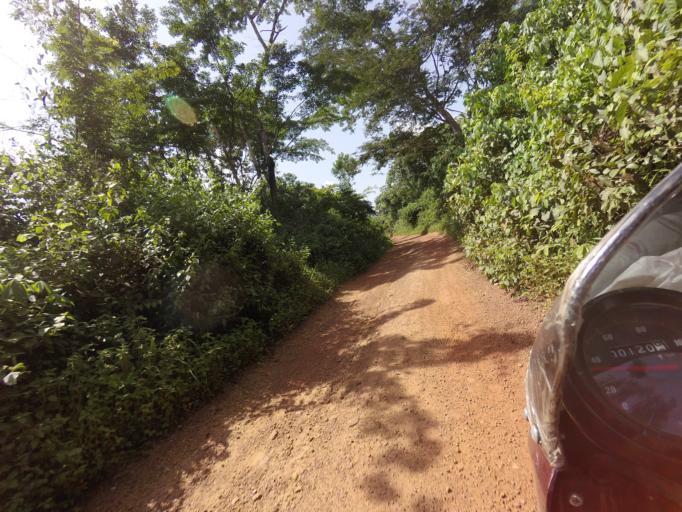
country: SL
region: Eastern Province
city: Manowa
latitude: 8.1637
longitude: -10.7507
